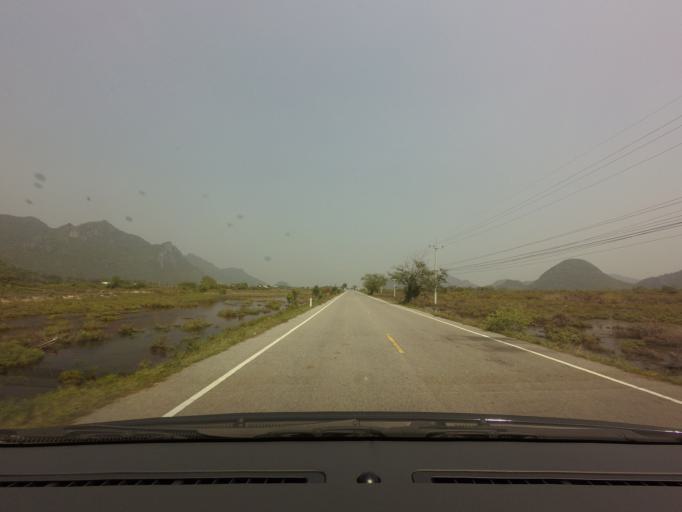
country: TH
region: Prachuap Khiri Khan
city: Sam Roi Yot
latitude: 12.1784
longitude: 99.9743
